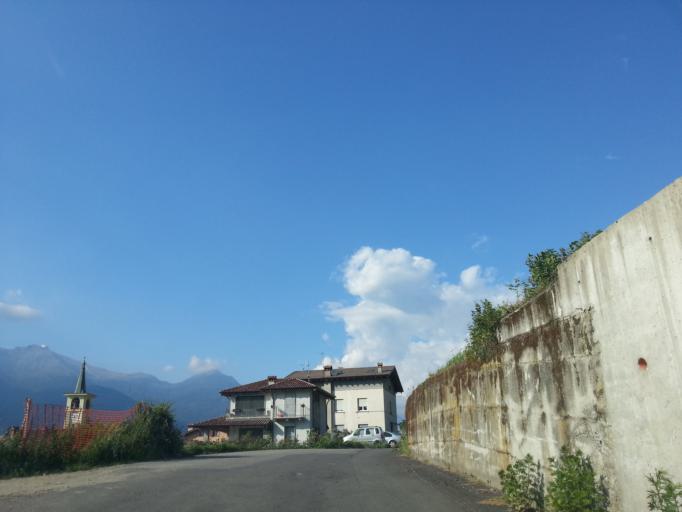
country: IT
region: Lombardy
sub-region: Provincia di Lecco
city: Colico Piano
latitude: 46.1225
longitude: 9.3595
